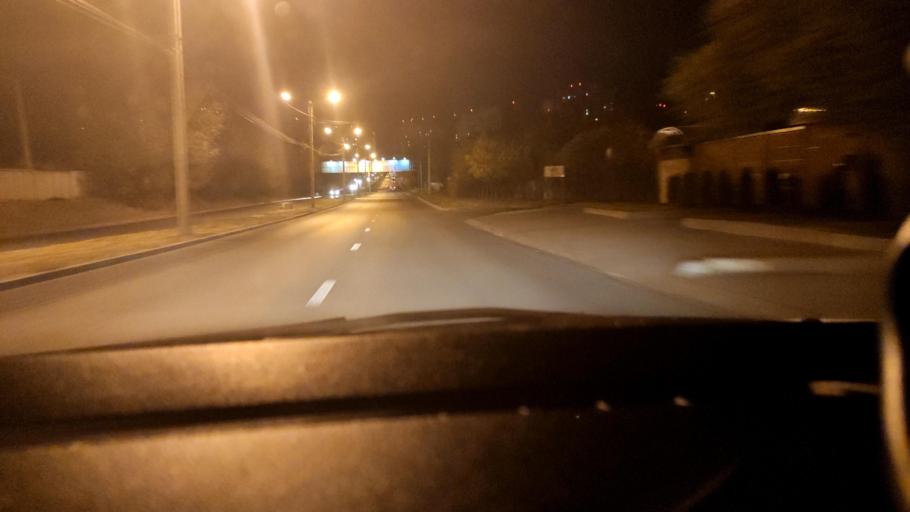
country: RU
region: Voronezj
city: Voronezh
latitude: 51.7070
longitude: 39.1956
